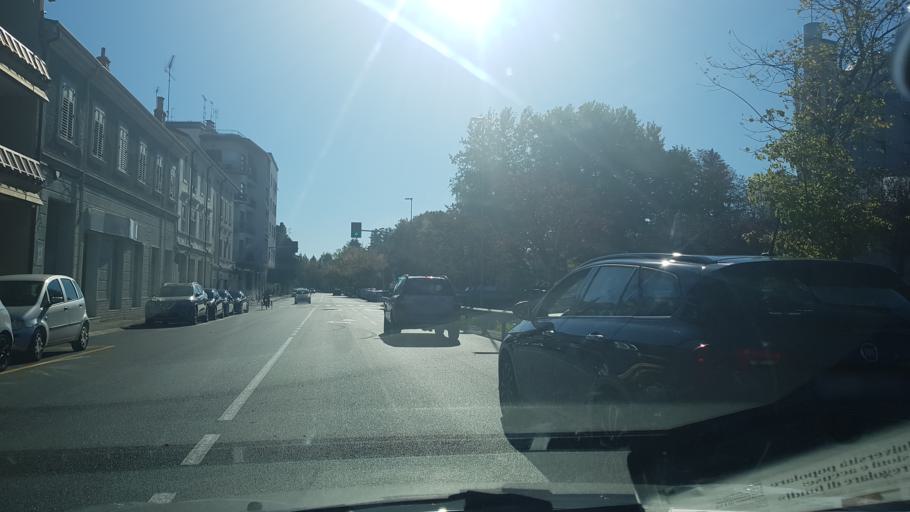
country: IT
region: Friuli Venezia Giulia
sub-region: Provincia di Gorizia
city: Monfalcone
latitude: 45.8067
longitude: 13.5283
